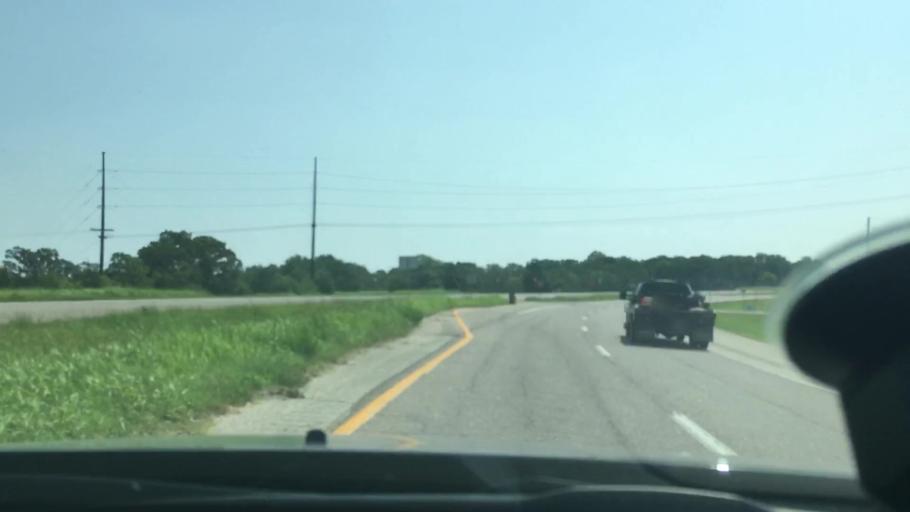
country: US
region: Oklahoma
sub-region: Pontotoc County
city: Ada
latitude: 34.7814
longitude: -96.6021
